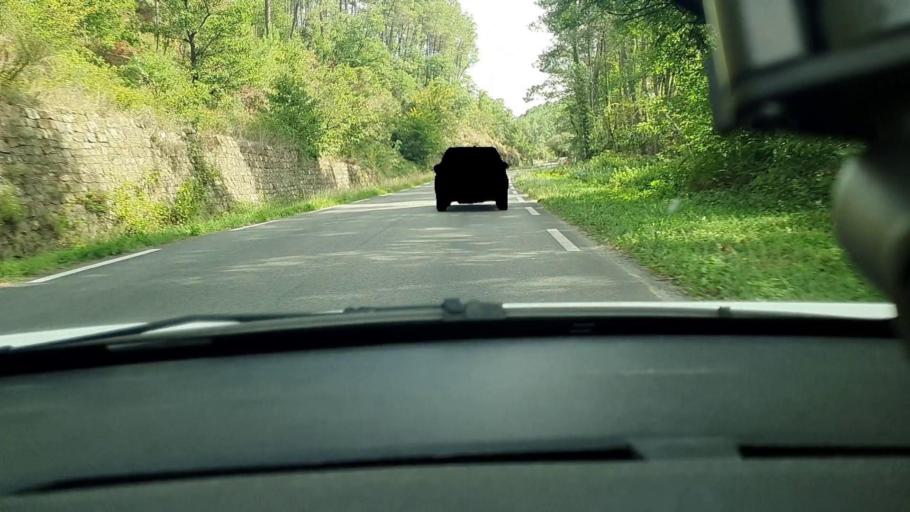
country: FR
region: Languedoc-Roussillon
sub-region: Departement du Gard
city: Saint-Florent-sur-Auzonnet
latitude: 44.2372
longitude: 4.1295
